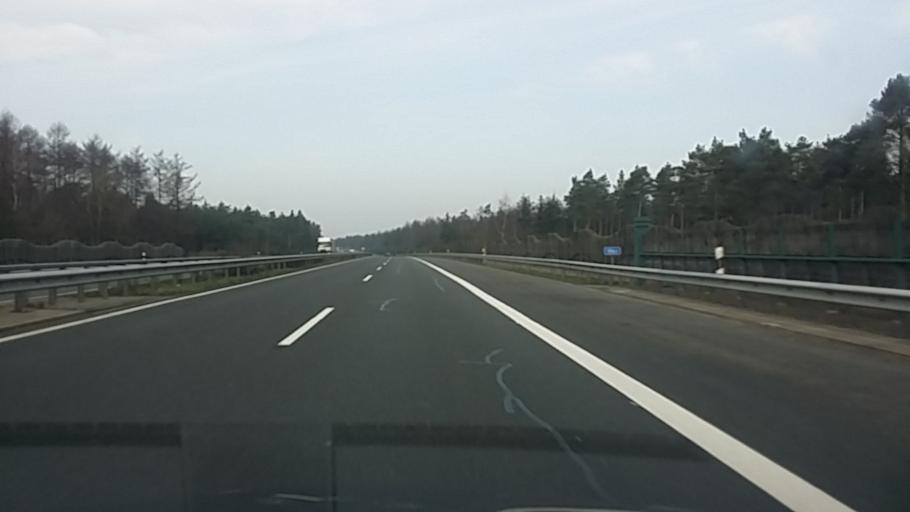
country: DE
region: Lower Saxony
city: Emsburen
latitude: 52.4489
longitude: 7.2506
